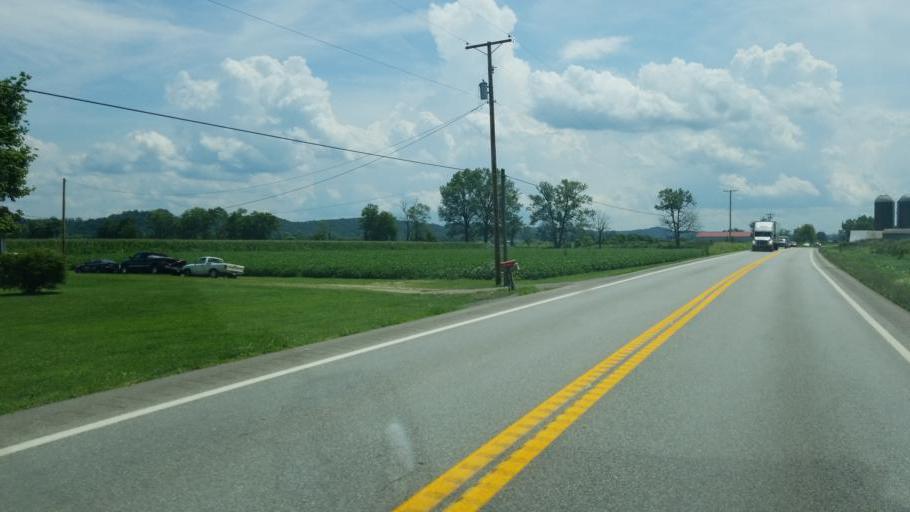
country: US
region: West Virginia
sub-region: Putnam County
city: Buffalo
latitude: 38.7145
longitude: -81.9682
